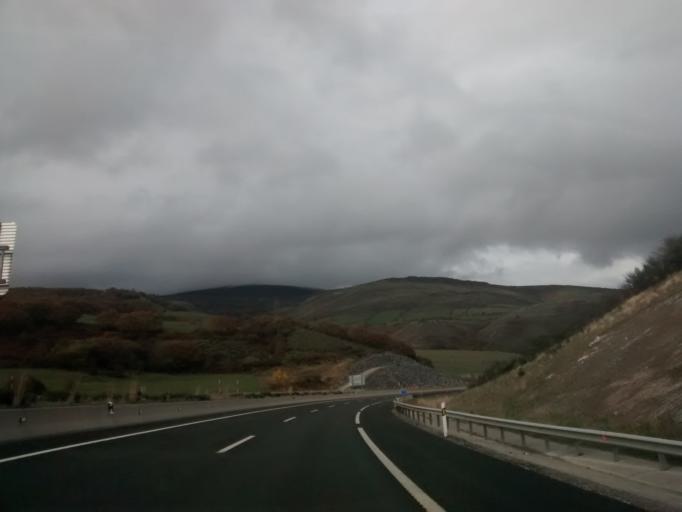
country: ES
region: Cantabria
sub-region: Provincia de Cantabria
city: Reinosa
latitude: 43.0158
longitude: -4.1247
